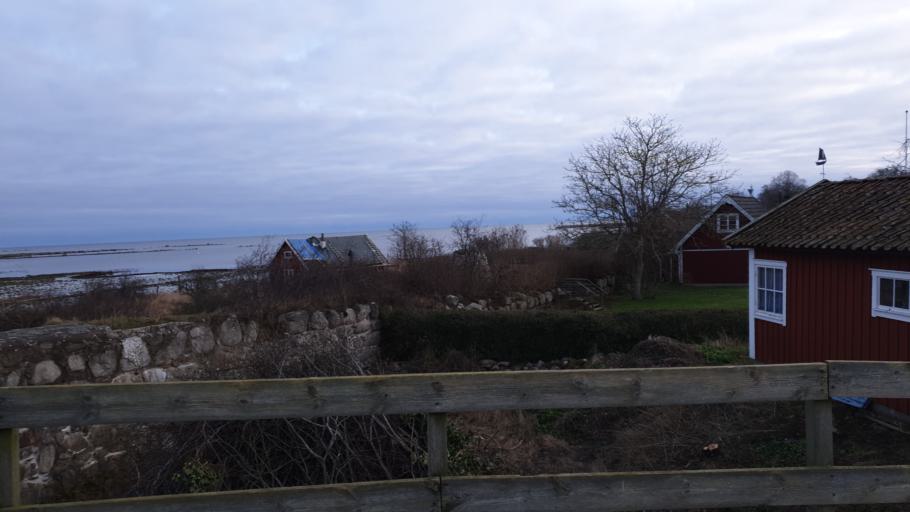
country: SE
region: Kalmar
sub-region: Torsas Kommun
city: Torsas
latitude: 56.2604
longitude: 16.0406
